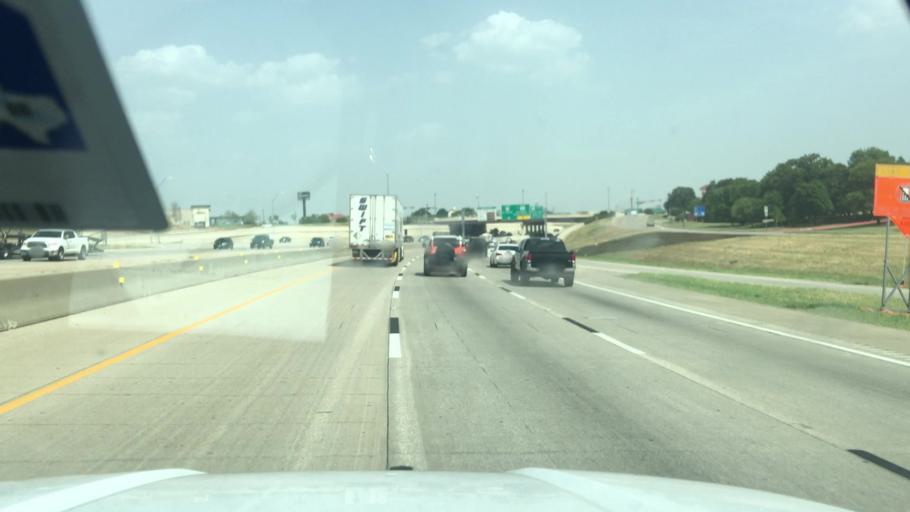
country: US
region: Texas
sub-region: Tarrant County
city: Grapevine
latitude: 32.9418
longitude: -97.1044
